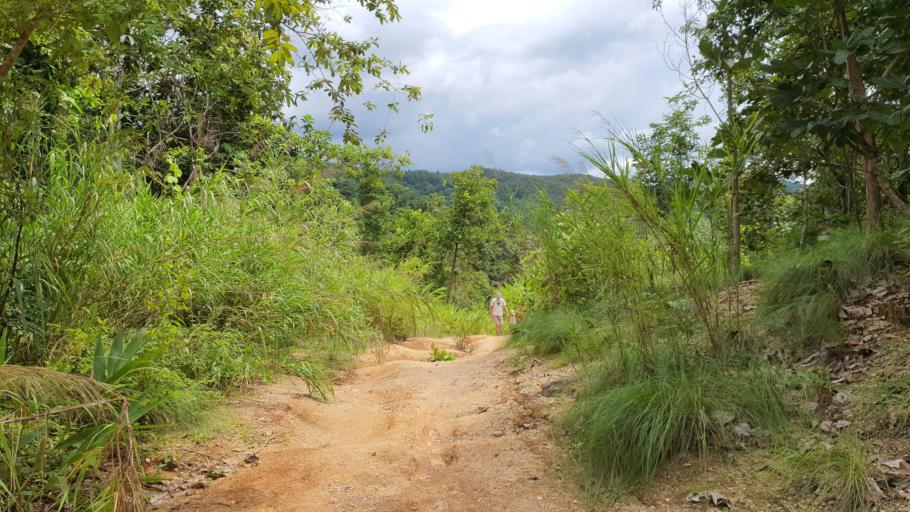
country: TH
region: Chiang Mai
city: Chiang Mai
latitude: 18.7671
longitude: 98.9104
